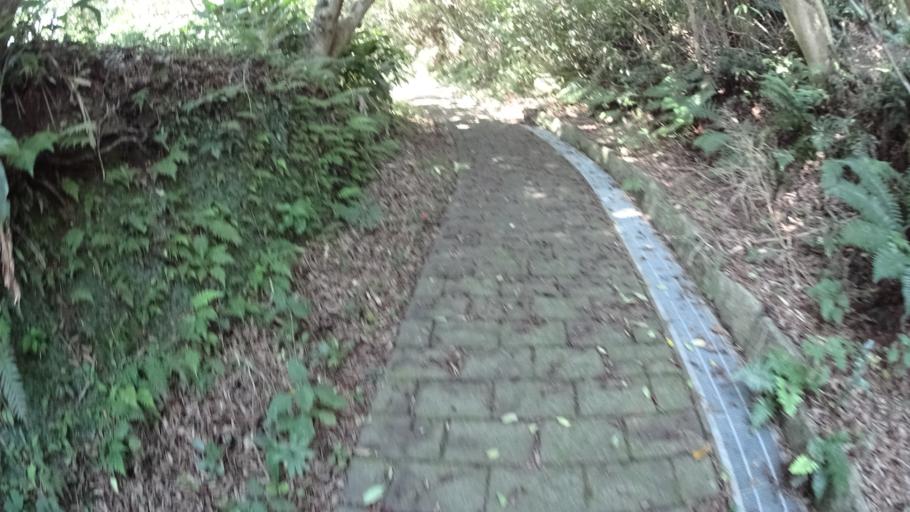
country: JP
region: Shizuoka
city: Shimoda
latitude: 34.5278
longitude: 139.2774
